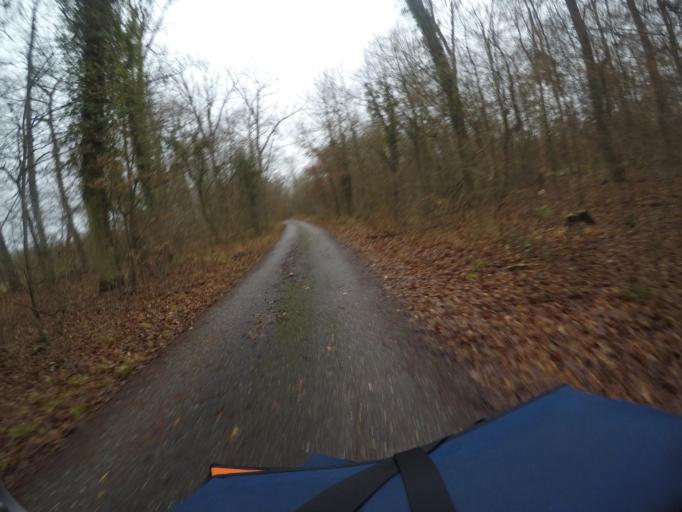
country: DE
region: Baden-Wuerttemberg
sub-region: Karlsruhe Region
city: Graben-Neudorf
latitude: 49.1963
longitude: 8.5014
